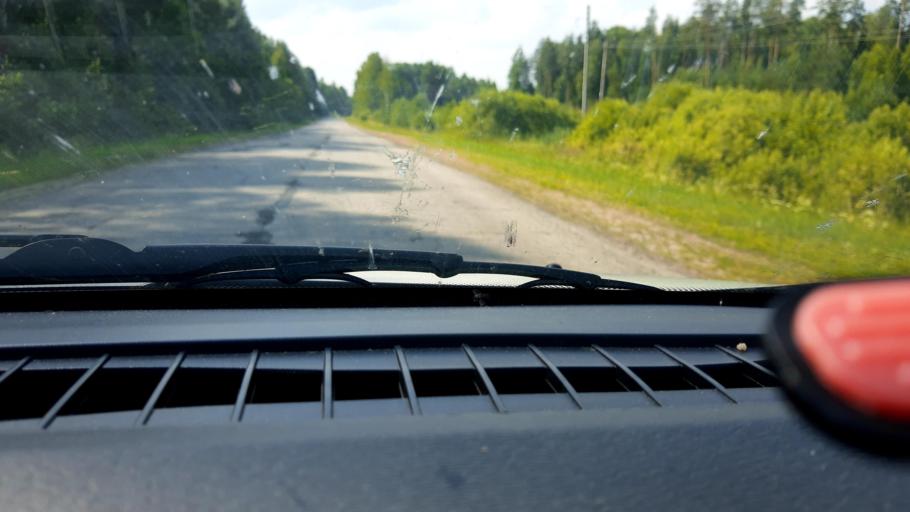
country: RU
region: Nizjnij Novgorod
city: Prudy
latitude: 57.3762
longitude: 46.1496
